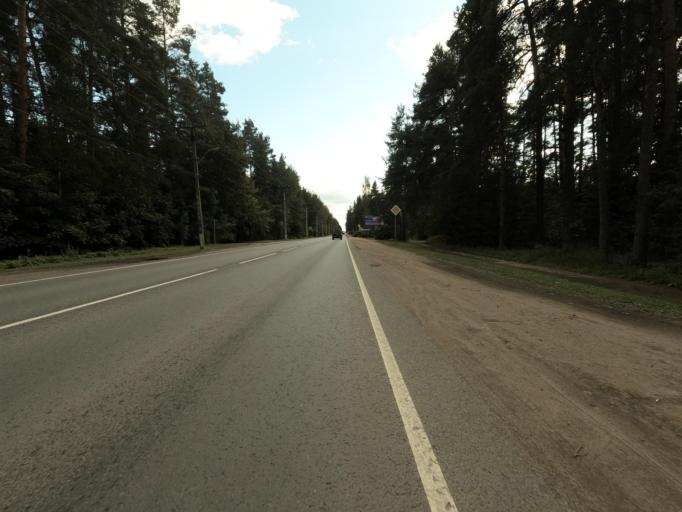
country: RU
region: Leningrad
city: Vsevolozhsk
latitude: 60.0063
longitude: 30.6642
